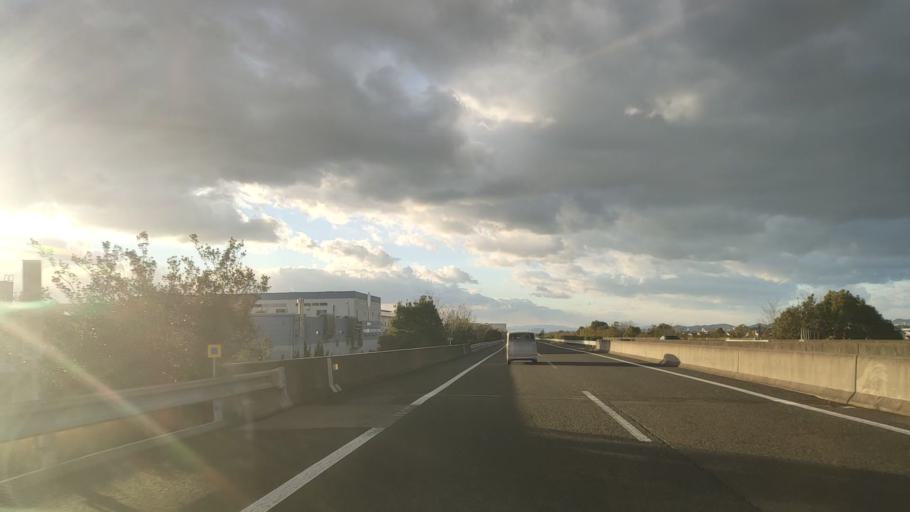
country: JP
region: Ehime
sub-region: Shikoku-chuo Shi
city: Matsuyama
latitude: 33.7853
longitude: 132.8446
